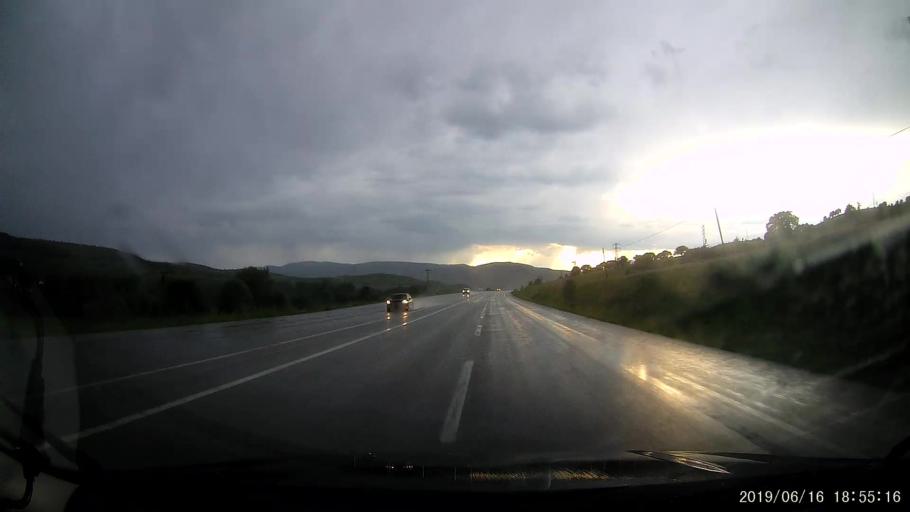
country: TR
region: Erzincan
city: Refahiye
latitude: 39.8994
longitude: 38.8322
